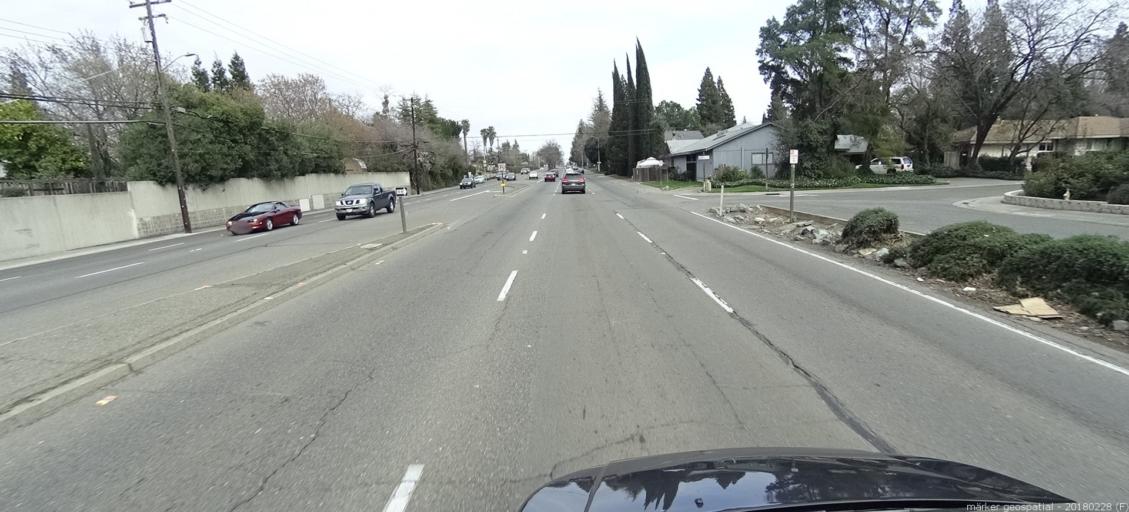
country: US
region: California
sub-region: Sacramento County
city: Fair Oaks
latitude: 38.6637
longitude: -121.2819
